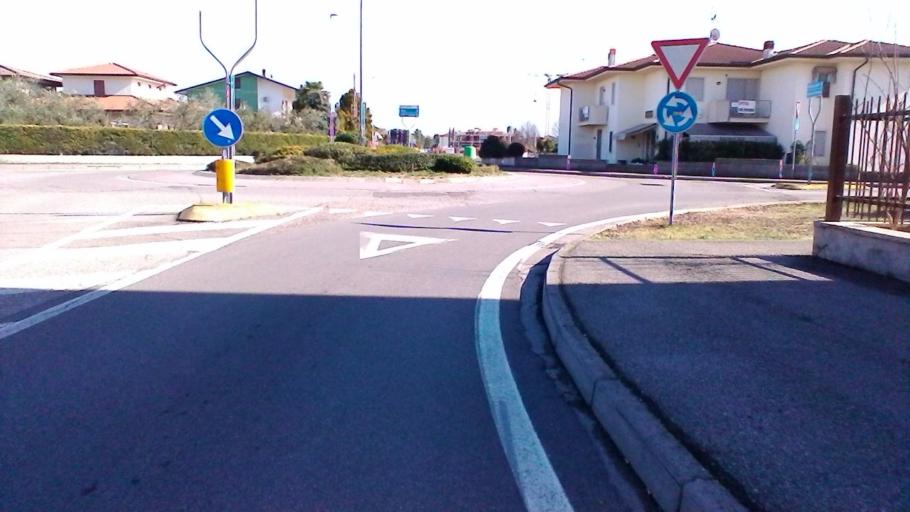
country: IT
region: Veneto
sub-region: Provincia di Verona
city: Alpo
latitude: 45.3739
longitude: 10.9206
